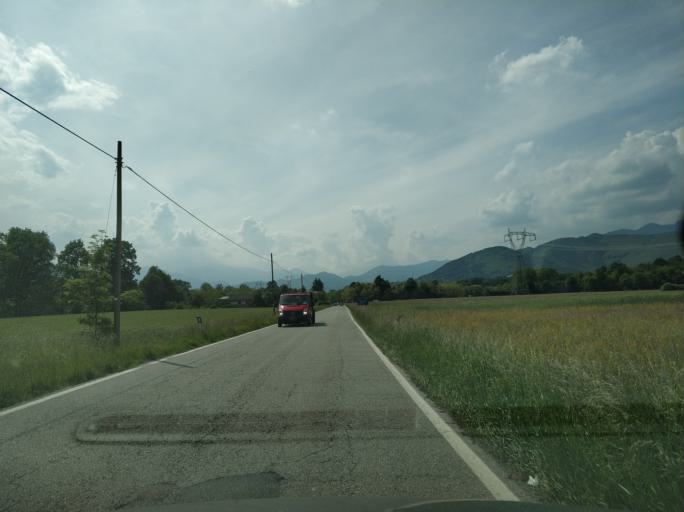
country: IT
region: Piedmont
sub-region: Provincia di Torino
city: Grosso
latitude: 45.2678
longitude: 7.5661
